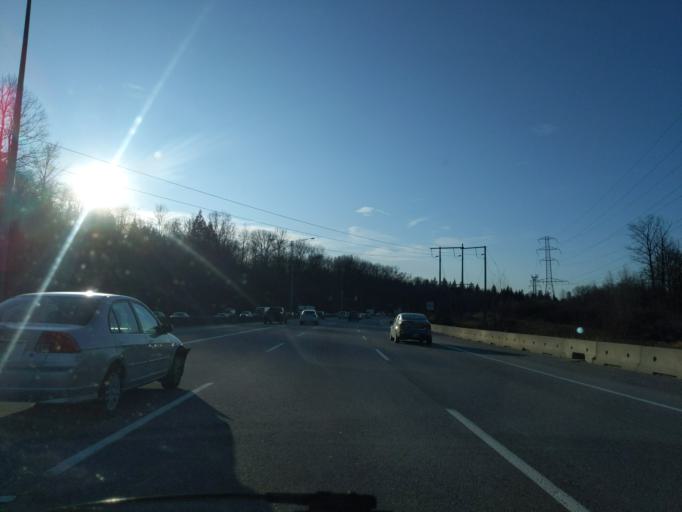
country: CA
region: British Columbia
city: New Westminster
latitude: 49.2382
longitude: -122.9234
